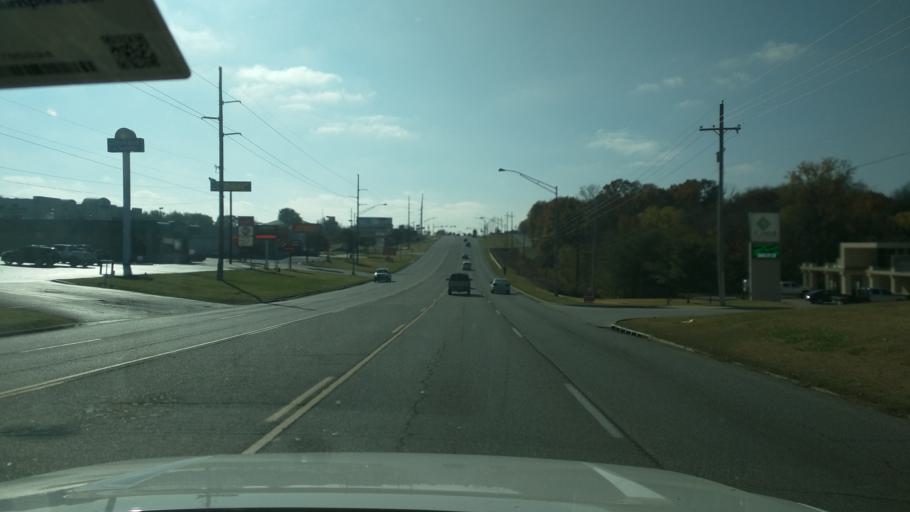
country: US
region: Oklahoma
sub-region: Washington County
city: Bartlesville
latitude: 36.7334
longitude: -95.9353
